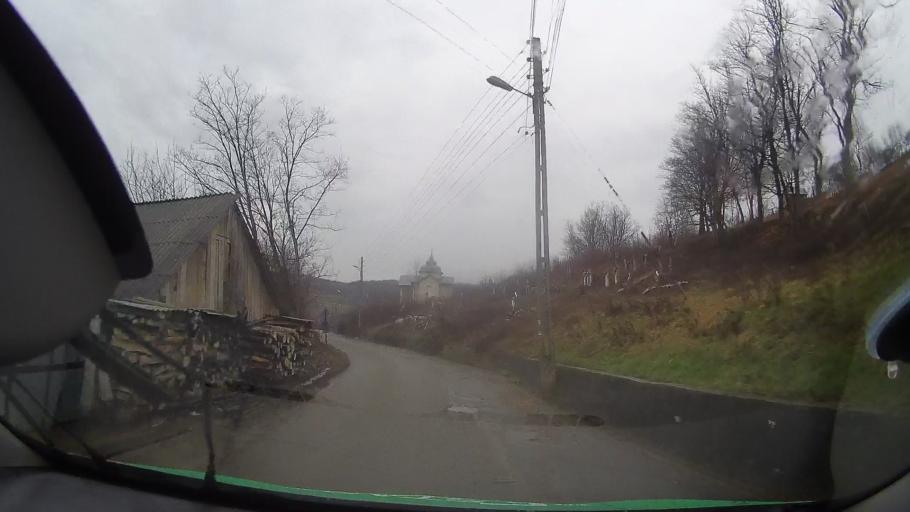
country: RO
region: Bihor
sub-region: Comuna Uileacu de Beius
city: Forau
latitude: 46.7129
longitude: 22.2287
